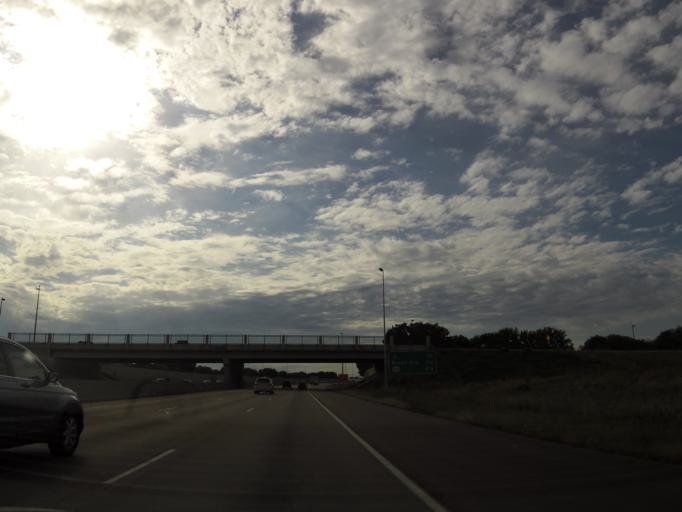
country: US
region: Minnesota
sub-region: Hennepin County
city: Brooklyn Park
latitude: 45.0763
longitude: -93.3542
